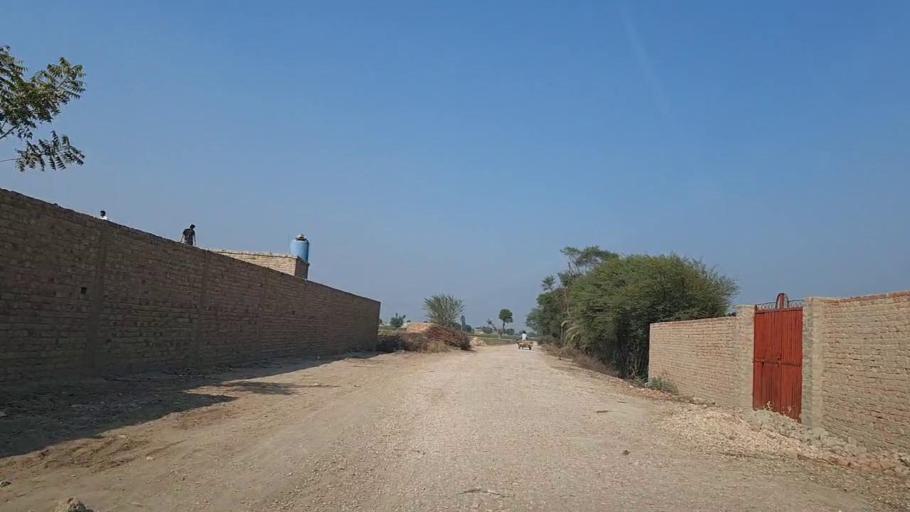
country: PK
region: Sindh
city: Moro
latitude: 26.6896
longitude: 67.9483
